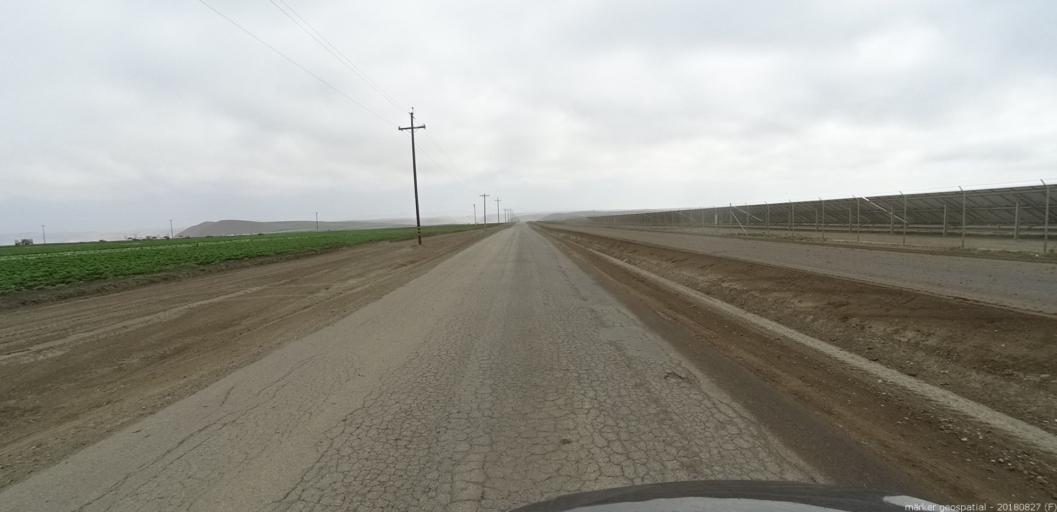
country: US
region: California
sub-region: Monterey County
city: King City
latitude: 36.2129
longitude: -121.0992
